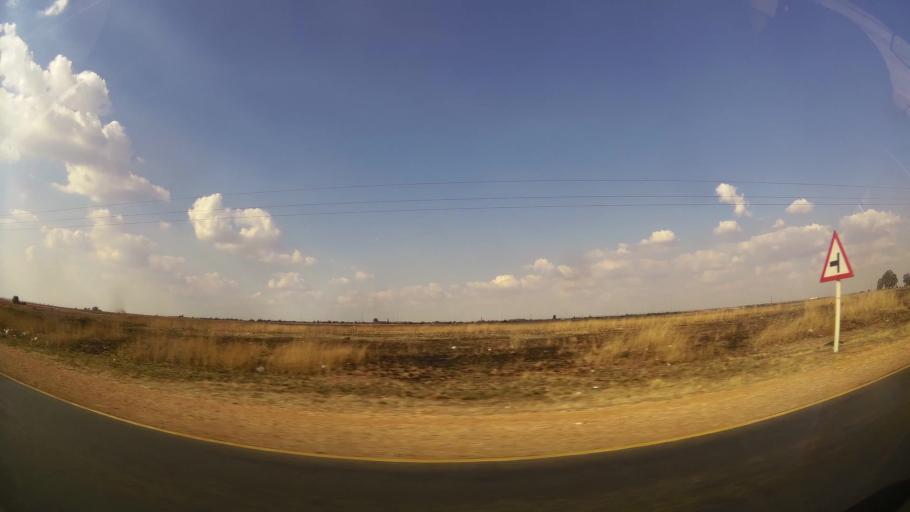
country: ZA
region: Gauteng
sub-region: Ekurhuleni Metropolitan Municipality
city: Springs
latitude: -26.3461
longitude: 28.3418
